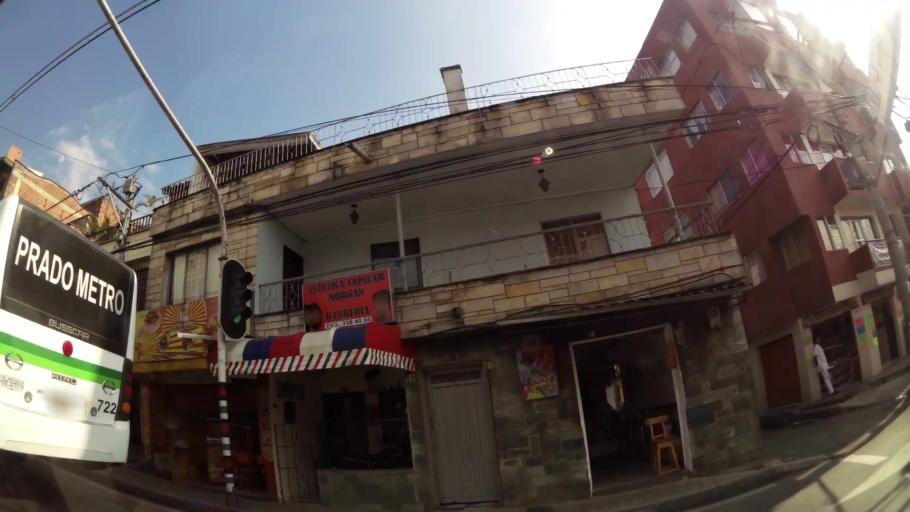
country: CO
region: Antioquia
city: La Estrella
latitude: 6.1742
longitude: -75.6338
